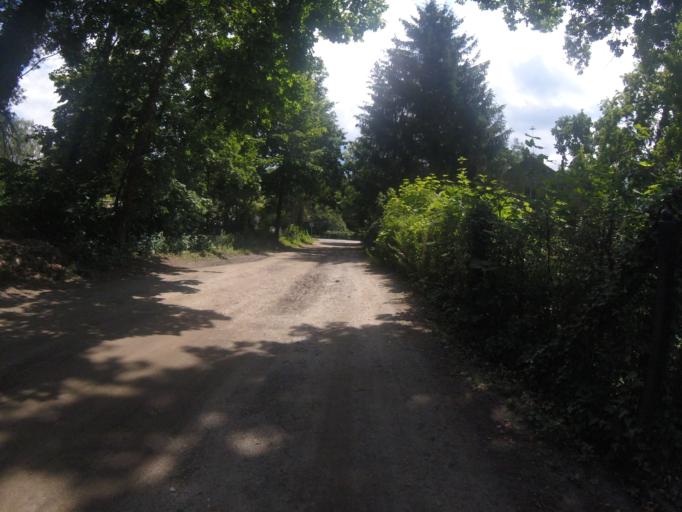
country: DE
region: Brandenburg
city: Bestensee
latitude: 52.2583
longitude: 13.6479
